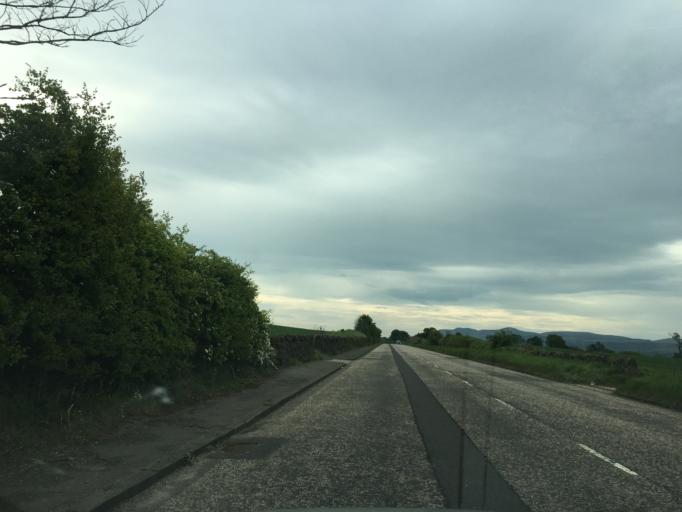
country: GB
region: Scotland
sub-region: Edinburgh
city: Ratho
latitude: 55.9489
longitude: -3.3321
